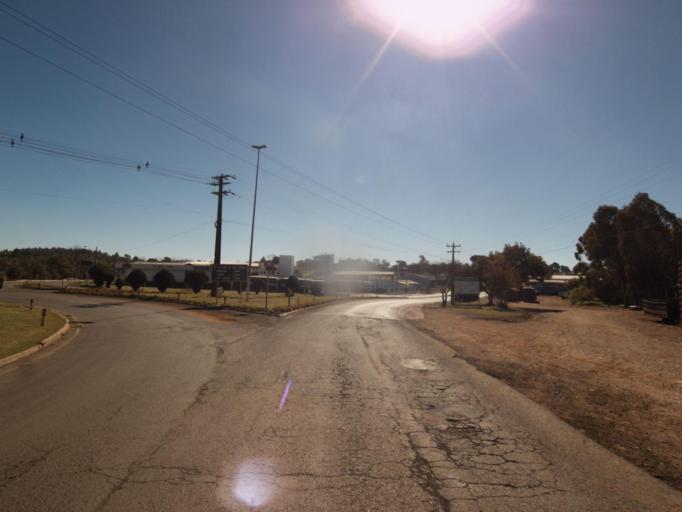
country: AR
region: Misiones
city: Bernardo de Irigoyen
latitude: -26.7611
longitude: -53.5002
